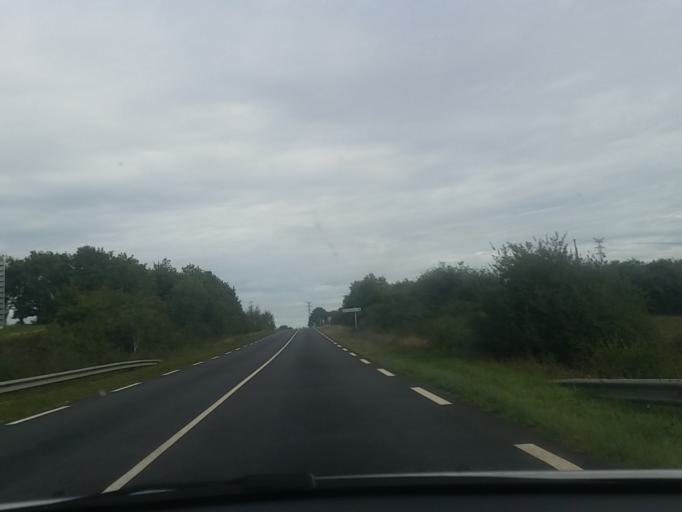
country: FR
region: Pays de la Loire
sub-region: Departement de la Loire-Atlantique
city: Chateaubriant
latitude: 47.7079
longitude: -1.3596
